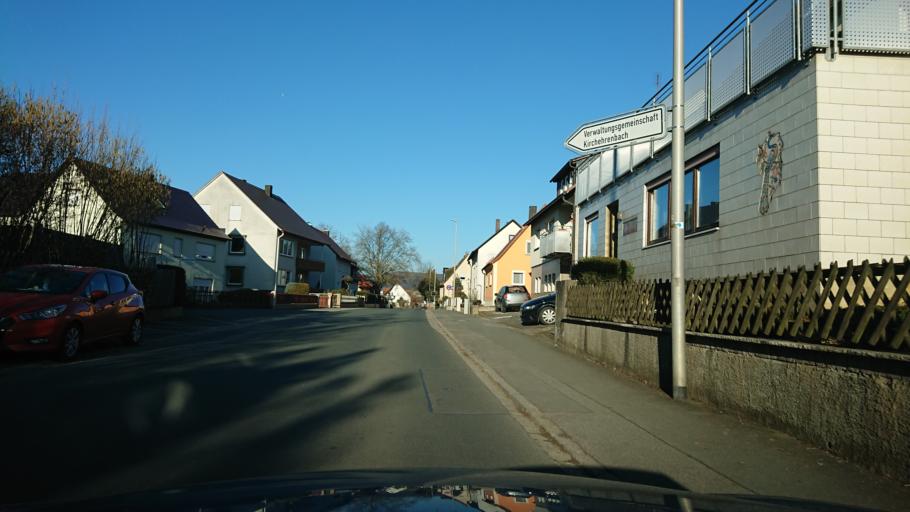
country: DE
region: Bavaria
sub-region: Upper Franconia
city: Kirchehrenbach
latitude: 49.7355
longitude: 11.1496
